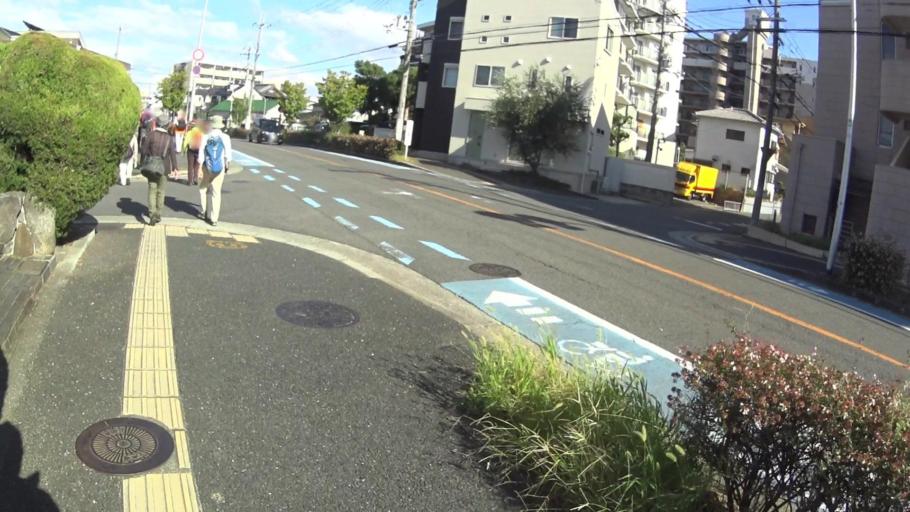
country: JP
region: Ehime
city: Kihoku-cho
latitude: 33.3930
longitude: 132.8504
